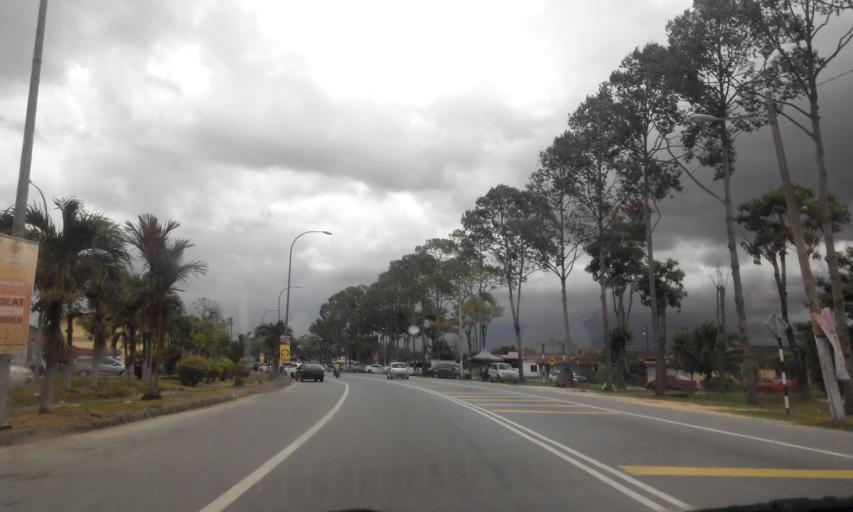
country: MY
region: Perak
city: Parit Buntar
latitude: 5.1125
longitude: 100.4881
